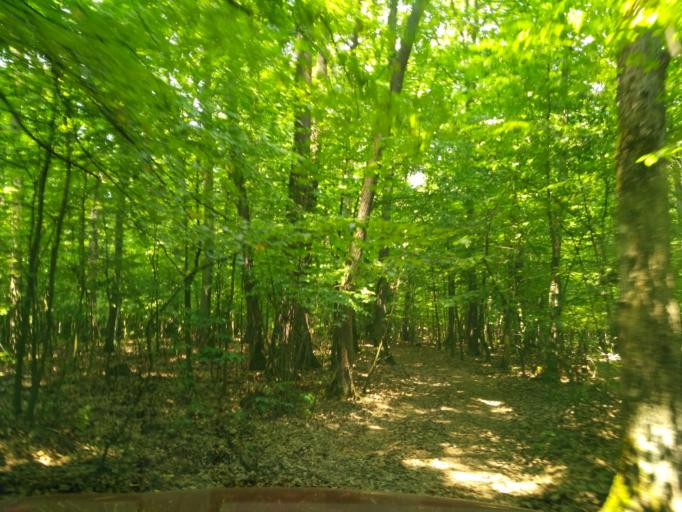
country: SK
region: Kosicky
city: Moldava nad Bodvou
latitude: 48.6482
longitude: 21.0355
